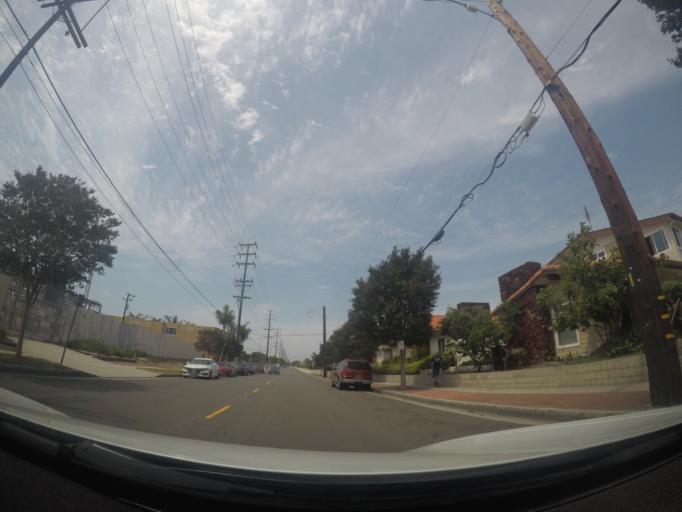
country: US
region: California
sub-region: Los Angeles County
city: Rolling Hills Estates
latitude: 33.8083
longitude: -118.3544
